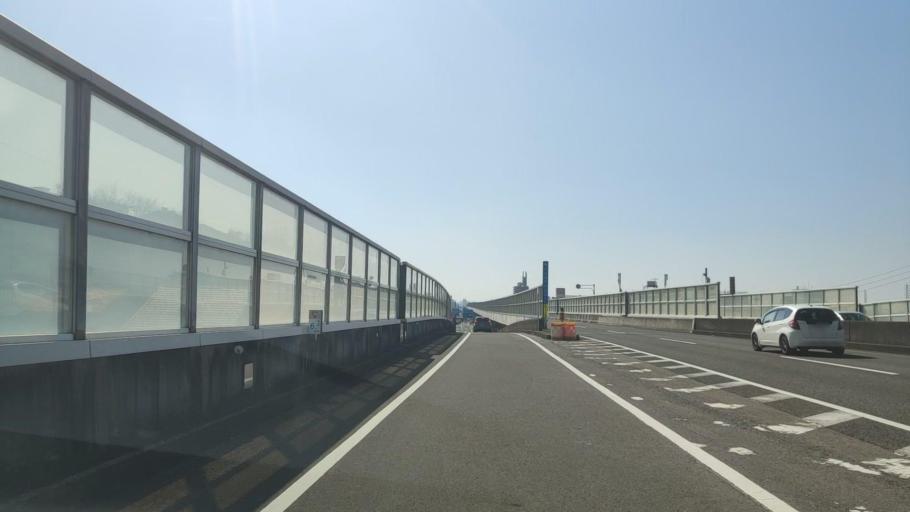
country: JP
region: Gifu
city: Gifu-shi
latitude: 35.4202
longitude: 136.7857
